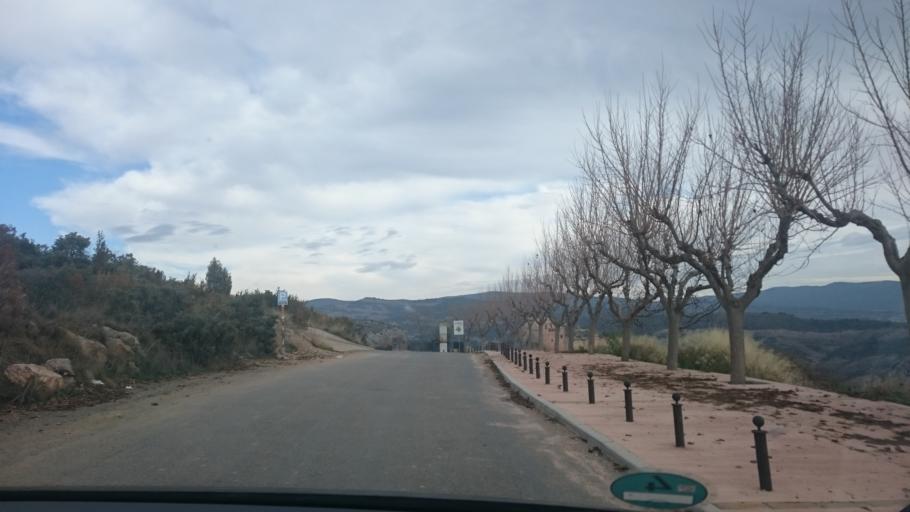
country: ES
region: Aragon
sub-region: Provincia de Huesca
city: Alquezar
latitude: 42.1695
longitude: 0.0221
